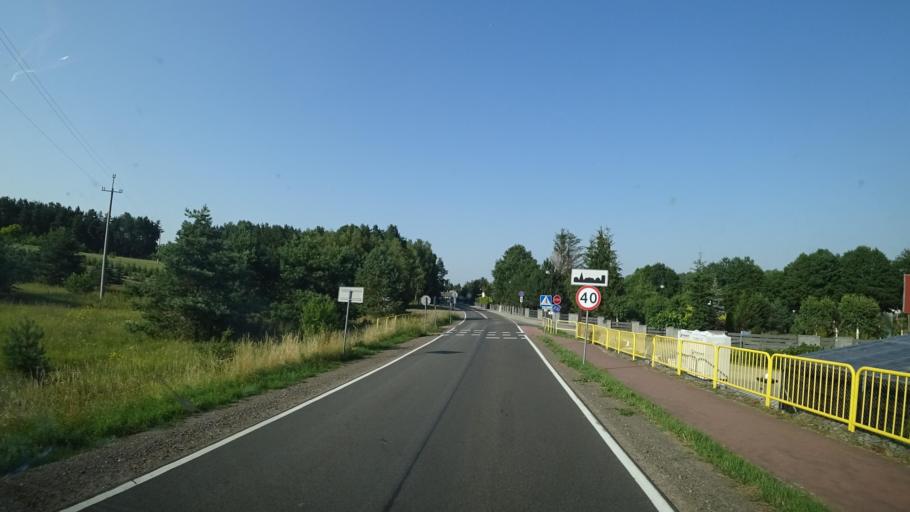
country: PL
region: Pomeranian Voivodeship
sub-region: Powiat bytowski
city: Lipnica
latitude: 53.8557
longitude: 17.4916
